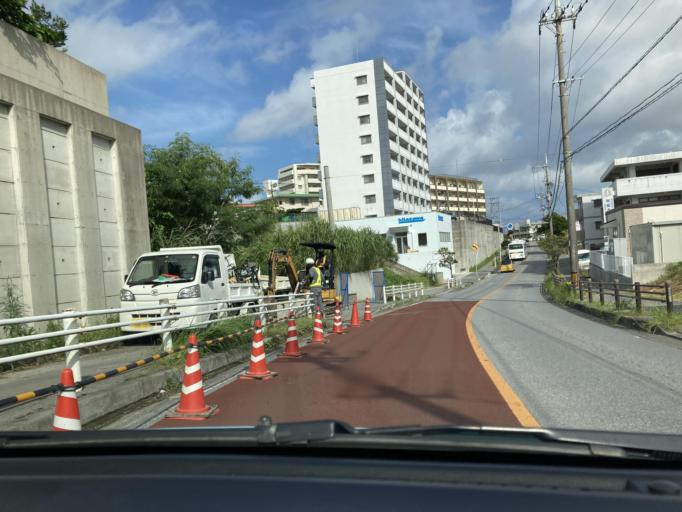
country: JP
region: Okinawa
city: Ginowan
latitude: 26.2563
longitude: 127.7692
